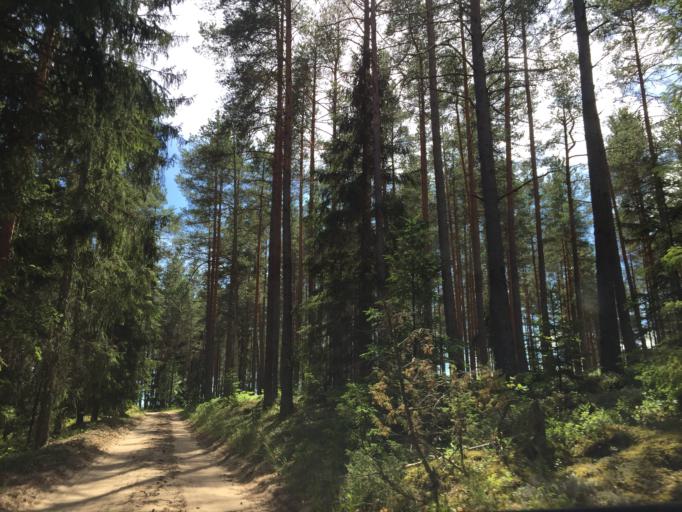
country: LV
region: Kuldigas Rajons
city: Kuldiga
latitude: 57.1123
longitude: 21.8774
